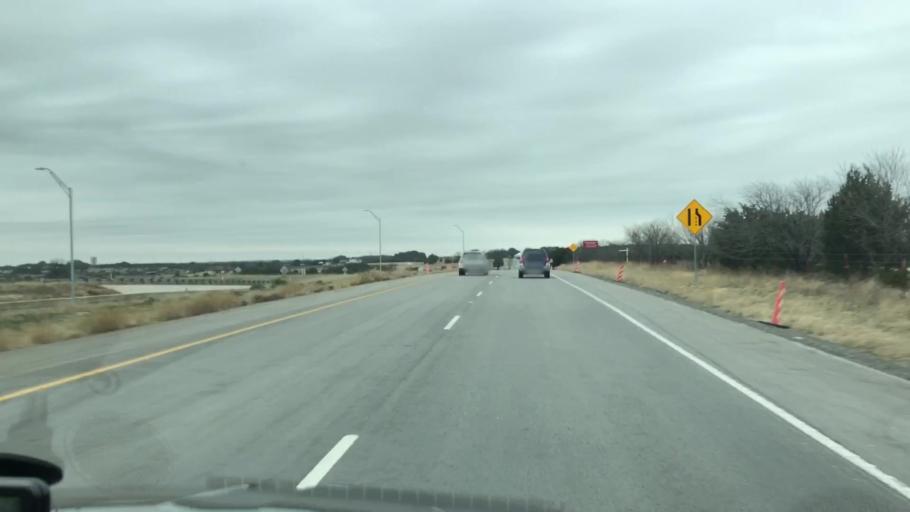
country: US
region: Texas
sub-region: Hamilton County
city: Hico
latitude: 32.0318
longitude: -98.0815
